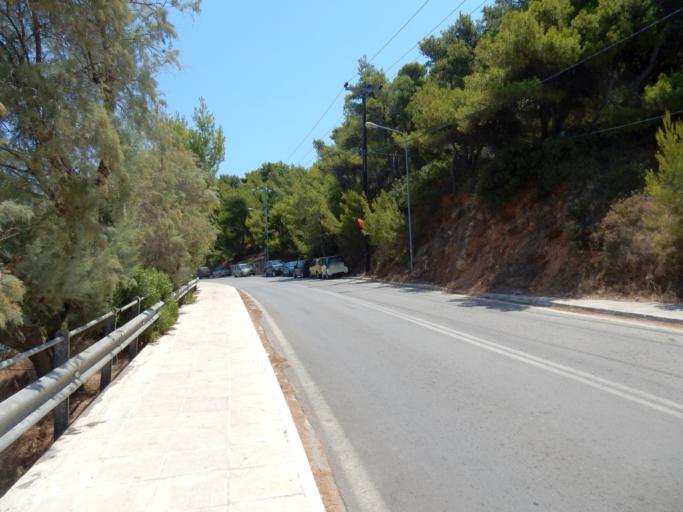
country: GR
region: Attica
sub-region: Nomarchia Anatolikis Attikis
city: Kalamos
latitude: 38.2968
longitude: 23.8865
